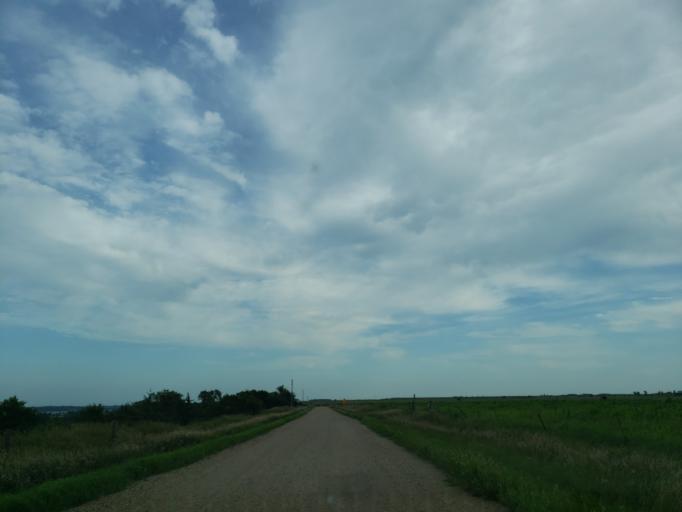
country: US
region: South Dakota
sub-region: Davison County
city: Mitchell
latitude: 43.6876
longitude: -97.9725
